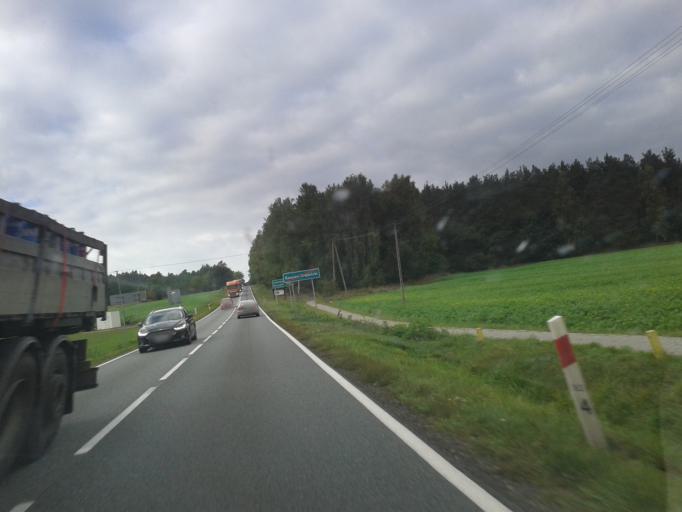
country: PL
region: Kujawsko-Pomorskie
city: Kamien Krajenski
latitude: 53.5429
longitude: 17.5150
